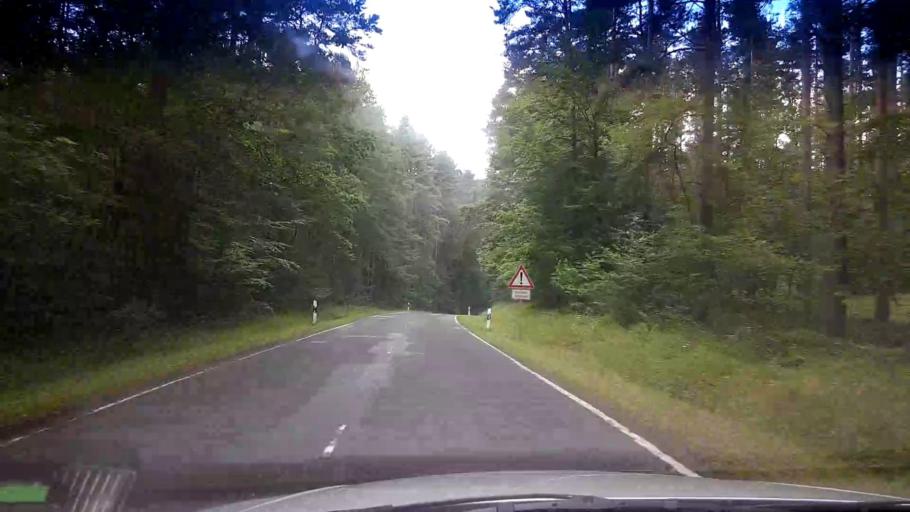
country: DE
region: Bavaria
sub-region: Upper Franconia
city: Oberhaid
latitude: 49.9482
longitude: 10.8141
